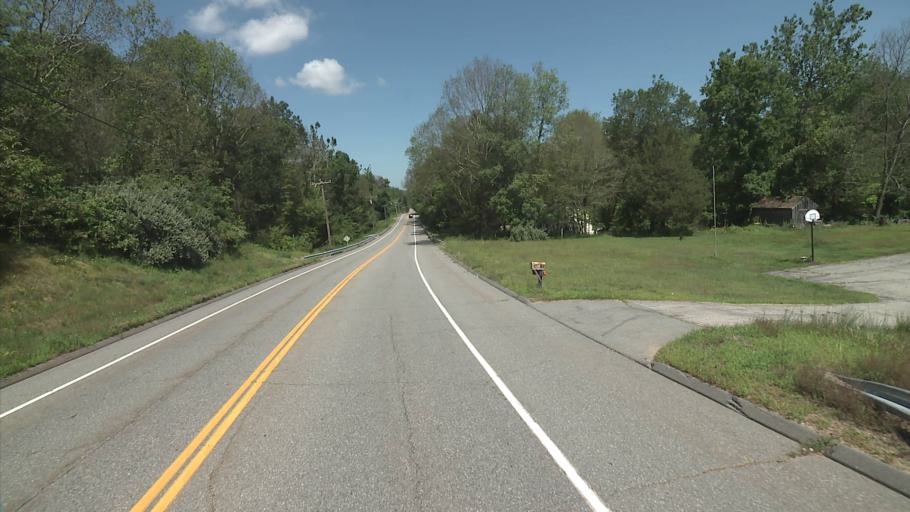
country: US
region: Connecticut
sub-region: Windham County
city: Plainfield Village
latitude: 41.6897
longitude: -71.9520
